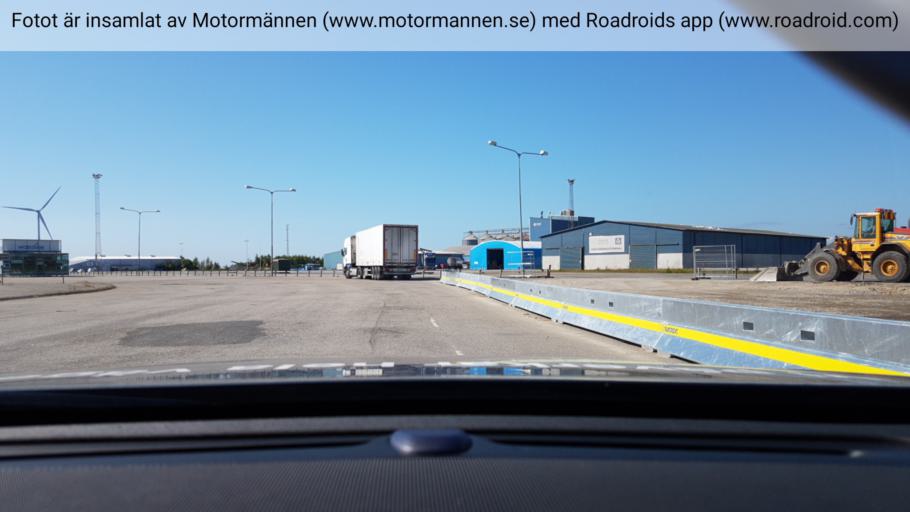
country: SE
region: Vaesterbotten
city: Obbola
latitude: 63.6842
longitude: 20.3398
